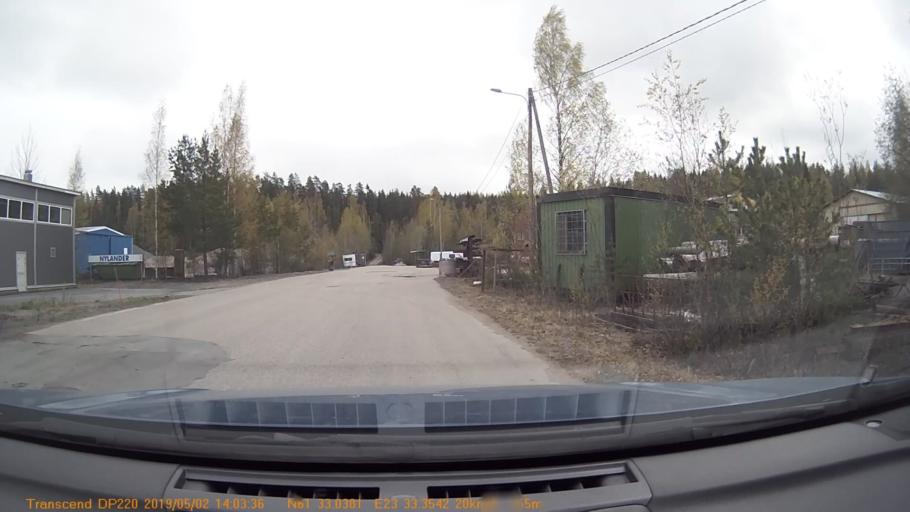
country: FI
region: Pirkanmaa
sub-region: Tampere
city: Yloejaervi
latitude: 61.5506
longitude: 23.5559
